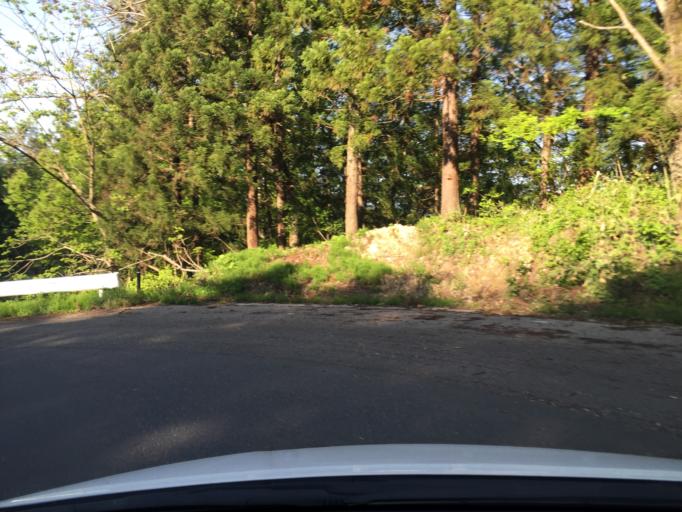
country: JP
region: Fukushima
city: Kitakata
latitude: 37.6762
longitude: 139.8047
